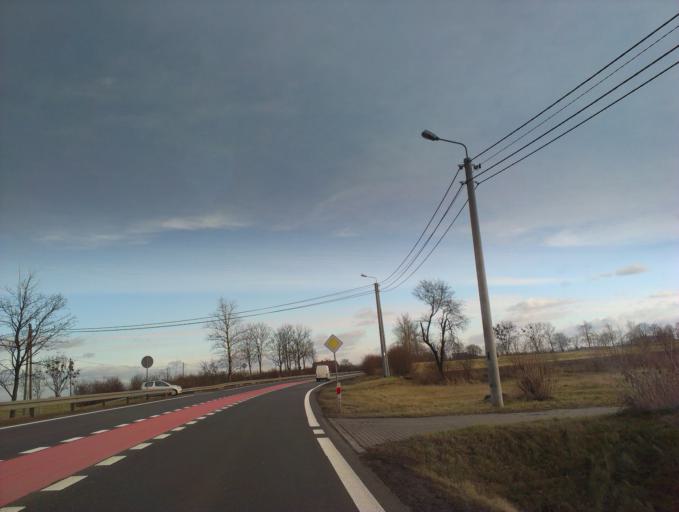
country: PL
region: Kujawsko-Pomorskie
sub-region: Powiat torunski
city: Czernikowo
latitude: 52.9332
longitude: 19.0167
